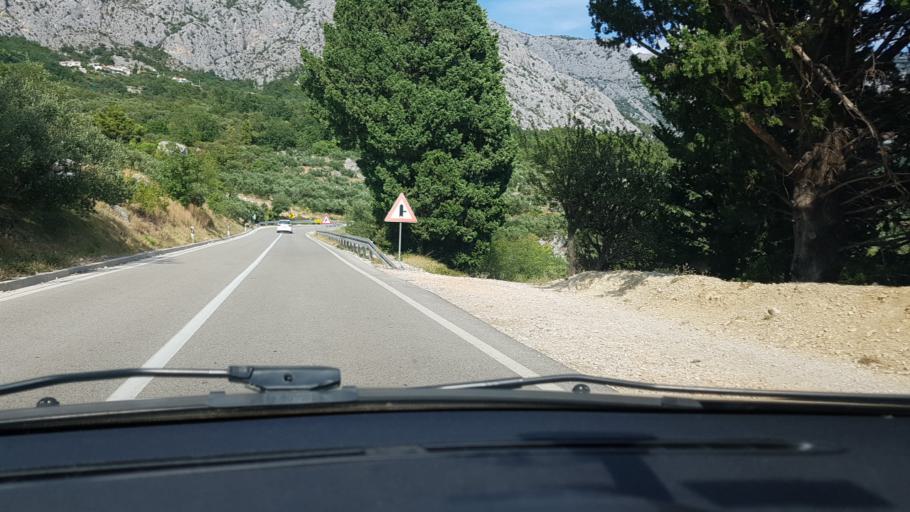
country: HR
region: Splitsko-Dalmatinska
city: Tucepi
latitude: 43.2788
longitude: 17.0563
